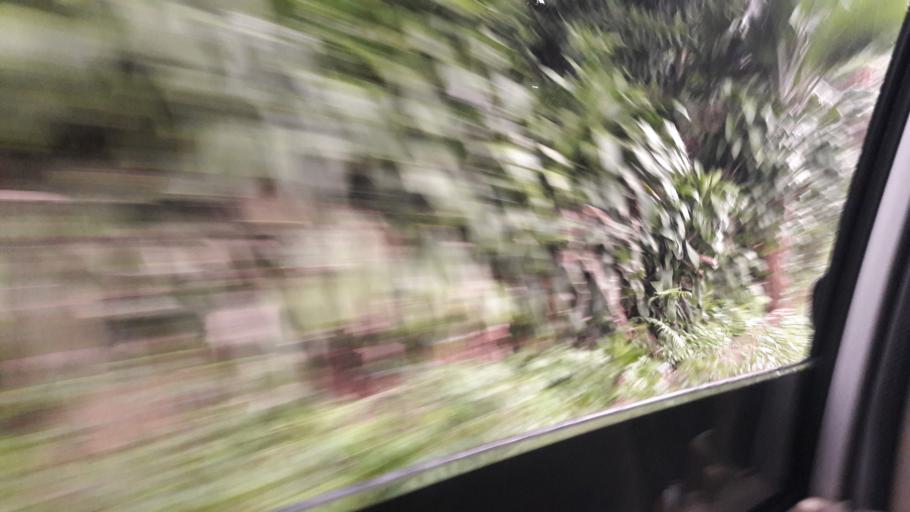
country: ID
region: West Java
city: Cipeundeuy
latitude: -6.6509
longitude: 106.5205
